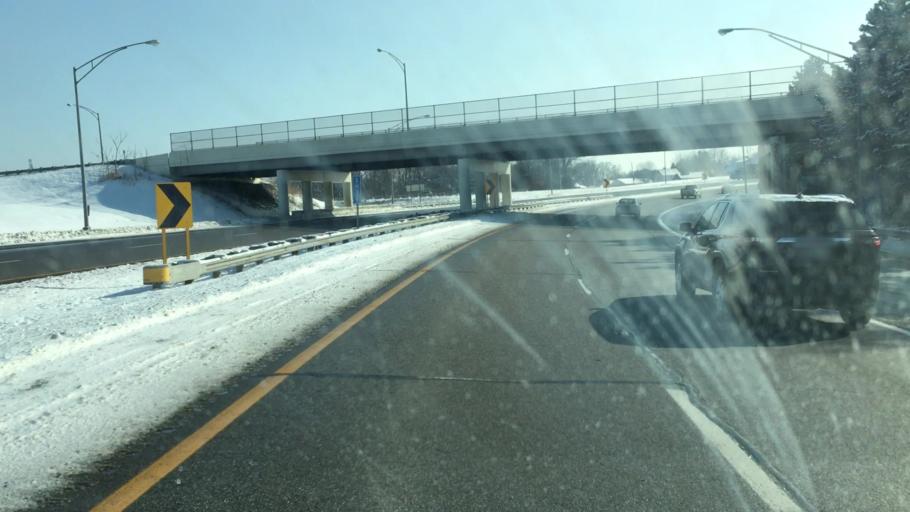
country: US
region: Ohio
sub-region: Trumbull County
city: Girard
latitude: 41.1184
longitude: -80.6950
